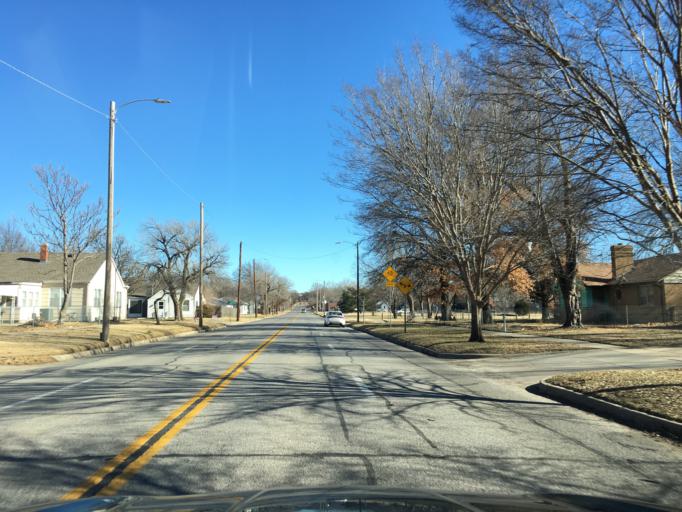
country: US
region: Kansas
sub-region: Sedgwick County
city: Wichita
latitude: 37.6718
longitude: -97.3023
